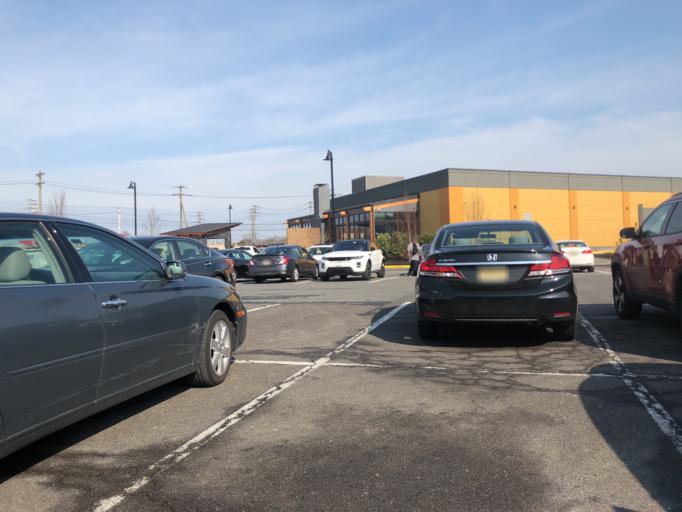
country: US
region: New Jersey
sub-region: Burlington County
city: Marlton
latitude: 39.8915
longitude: -74.9276
